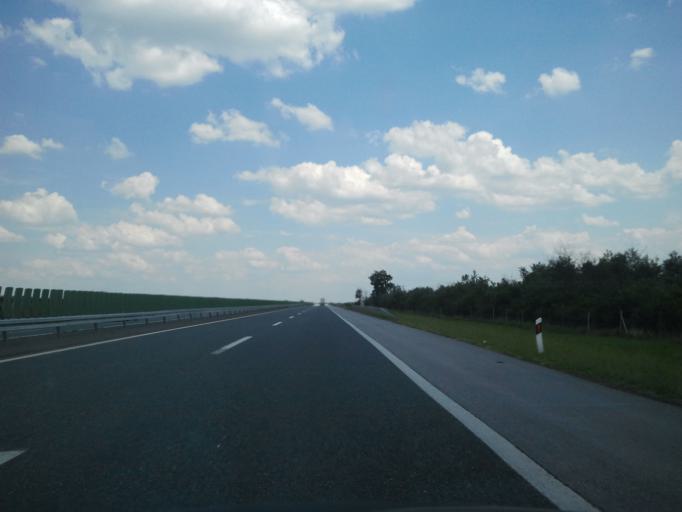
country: HR
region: Brodsko-Posavska
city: Bukovlje
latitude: 45.1736
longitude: 18.1189
